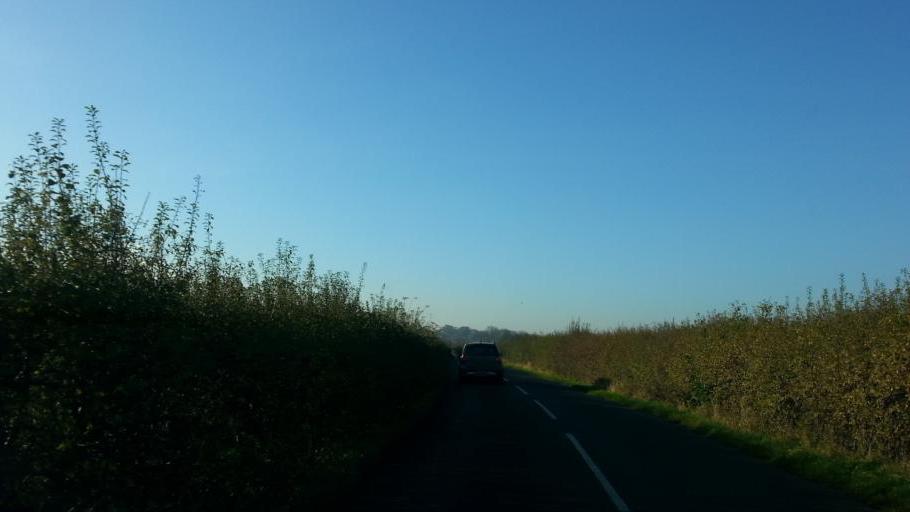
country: GB
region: England
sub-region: Nottinghamshire
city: Newark on Trent
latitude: 53.0976
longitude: -0.8418
